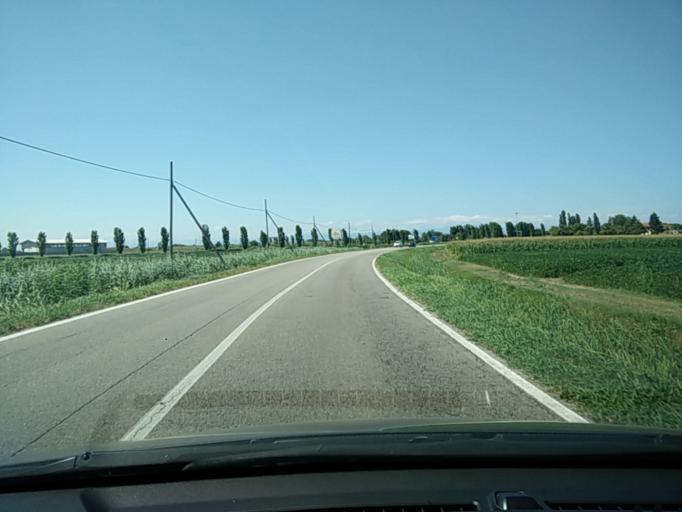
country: IT
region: Veneto
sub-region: Provincia di Venezia
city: La Salute di Livenza
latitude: 45.6388
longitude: 12.8452
